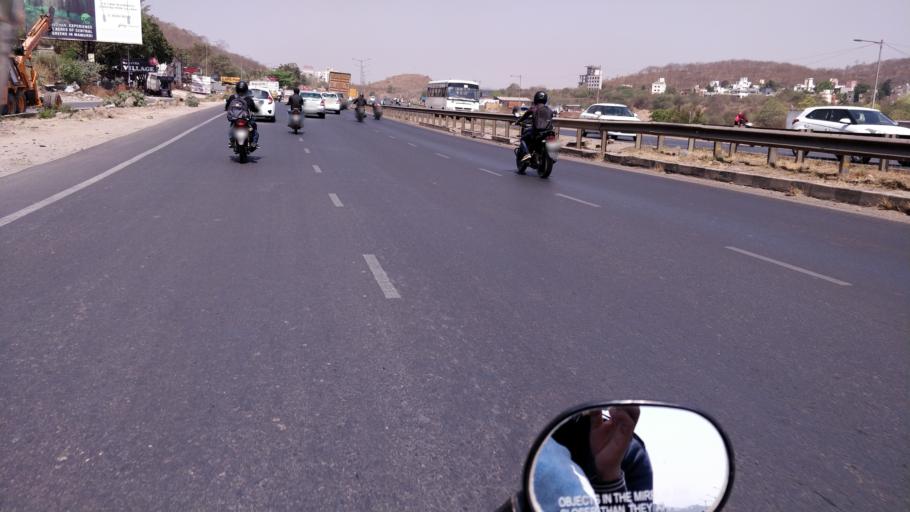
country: IN
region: Maharashtra
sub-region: Pune Division
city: Shivaji Nagar
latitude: 18.5415
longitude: 73.7782
